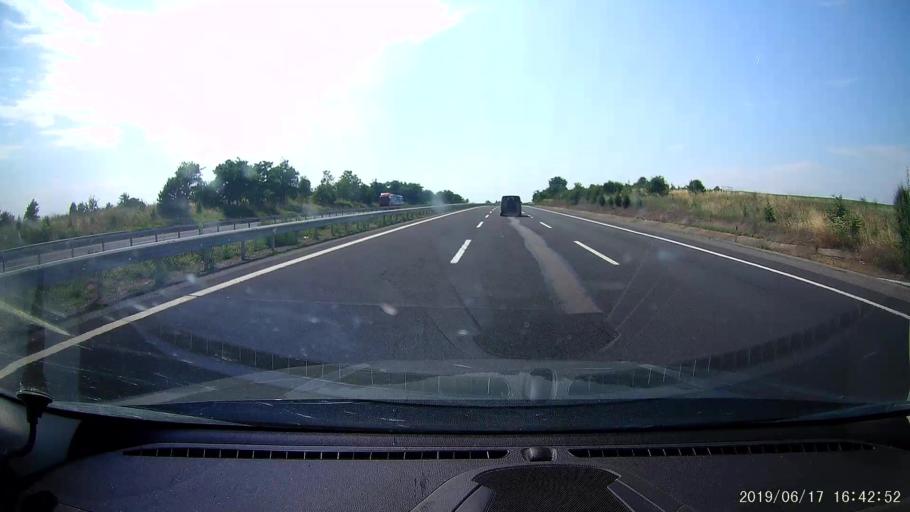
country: TR
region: Kirklareli
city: Luleburgaz
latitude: 41.4762
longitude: 27.3104
